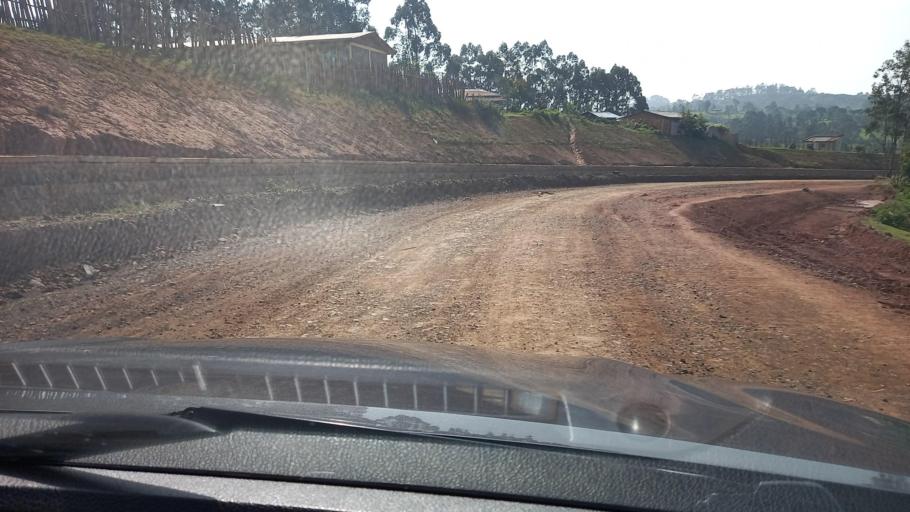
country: ET
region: Southern Nations, Nationalities, and People's Region
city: Mizan Teferi
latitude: 6.1740
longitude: 35.5853
